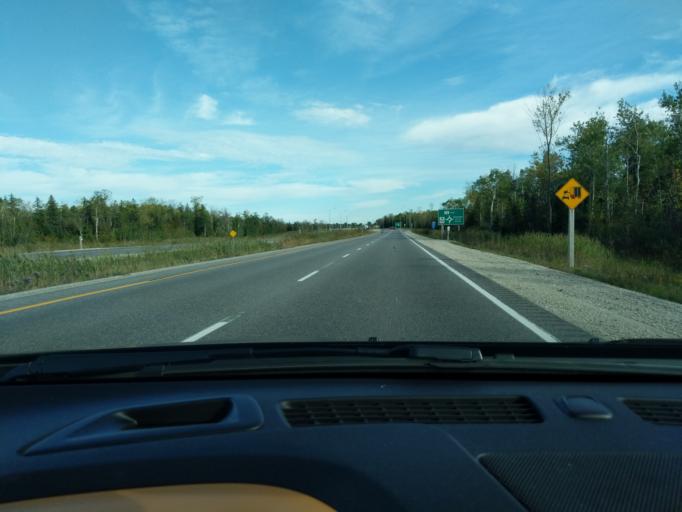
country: CA
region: Ontario
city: Collingwood
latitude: 44.4638
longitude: -80.1202
